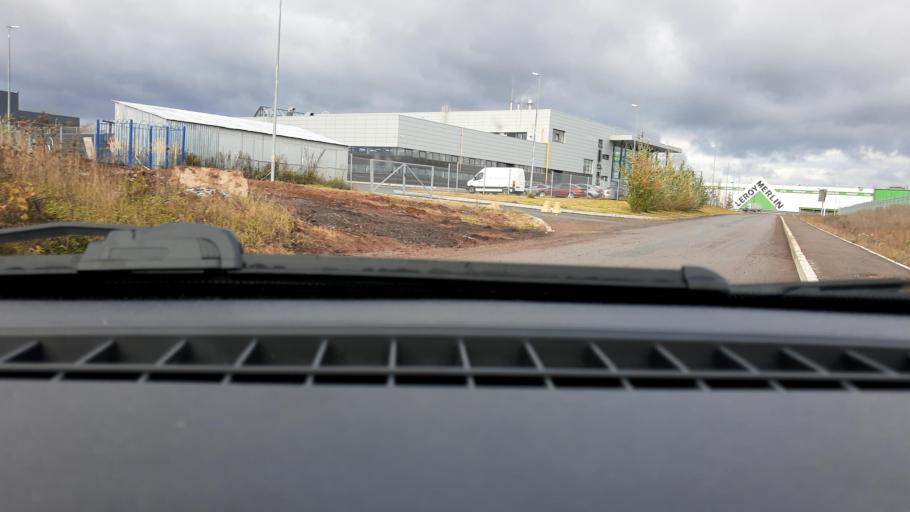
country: RU
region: Bashkortostan
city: Ufa
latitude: 54.6669
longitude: 55.9298
